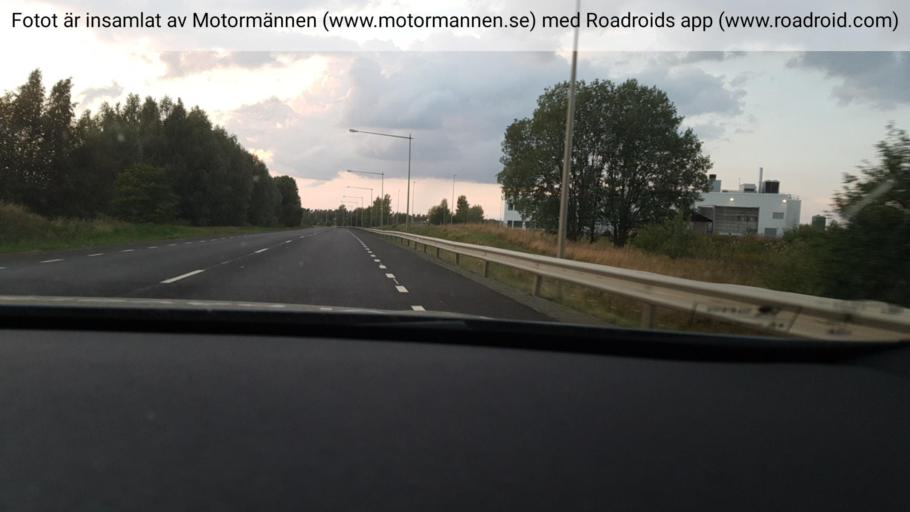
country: SE
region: Vaestra Goetaland
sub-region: Skovde Kommun
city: Skoevde
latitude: 58.3885
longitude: 13.8749
